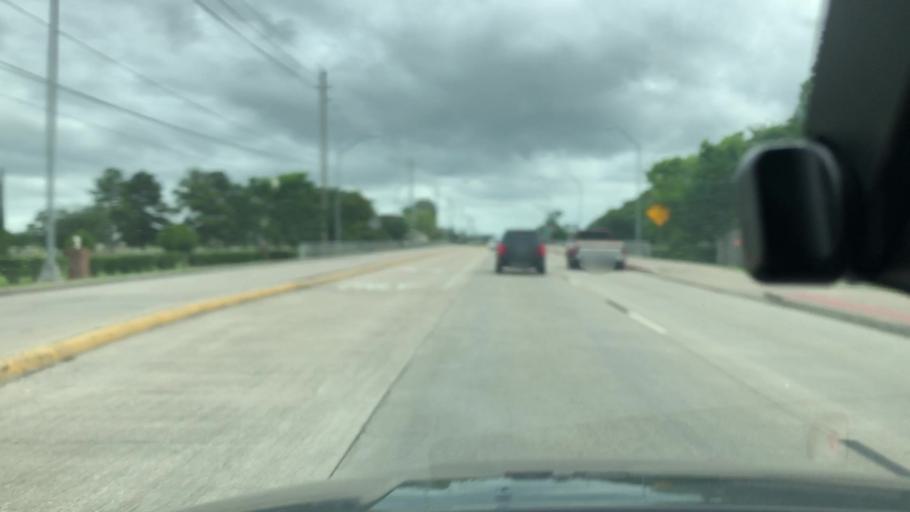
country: US
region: Texas
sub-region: Brazoria County
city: Brookside Village
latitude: 29.5682
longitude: -95.3507
